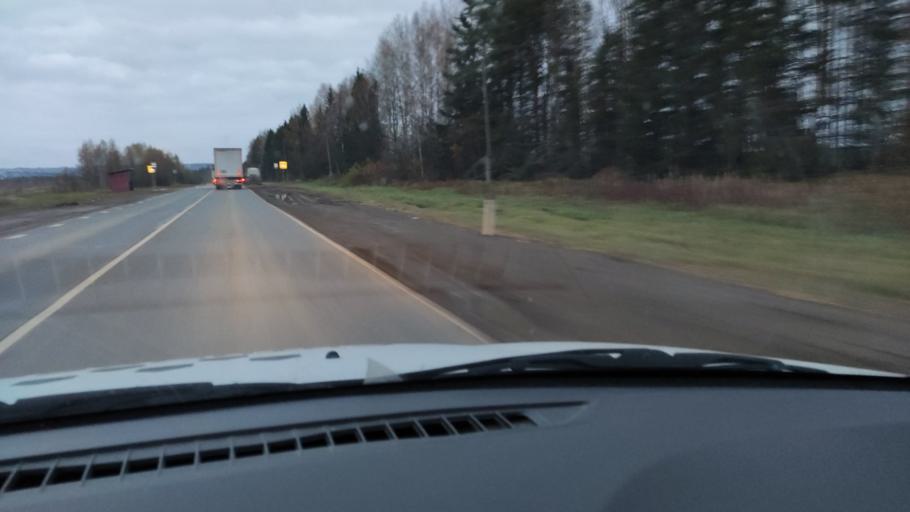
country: RU
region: Kirov
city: Kostino
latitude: 58.8578
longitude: 53.1844
